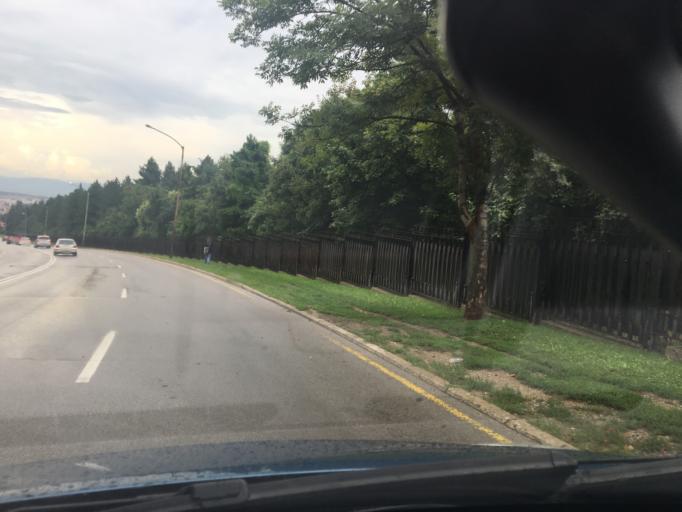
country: BG
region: Sofia-Capital
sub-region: Stolichna Obshtina
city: Sofia
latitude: 42.6509
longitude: 23.2662
